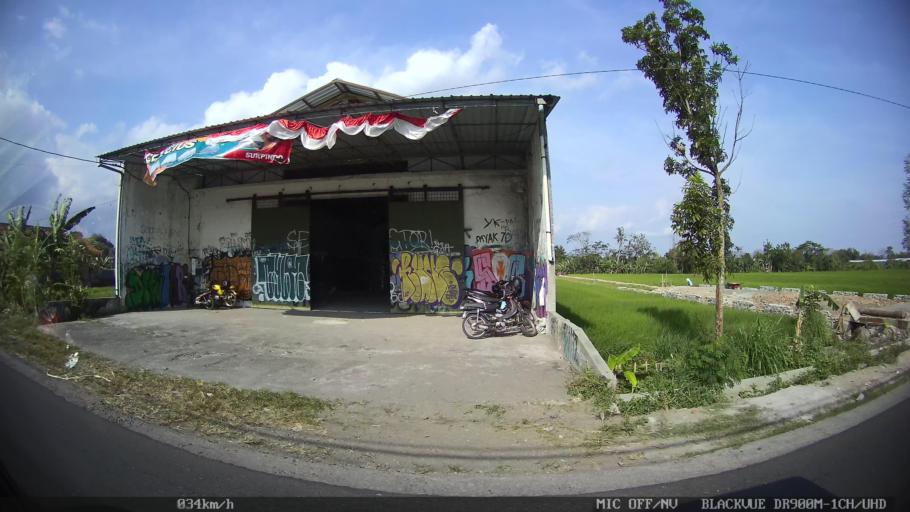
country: ID
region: Daerah Istimewa Yogyakarta
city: Kasihan
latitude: -7.8388
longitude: 110.3440
